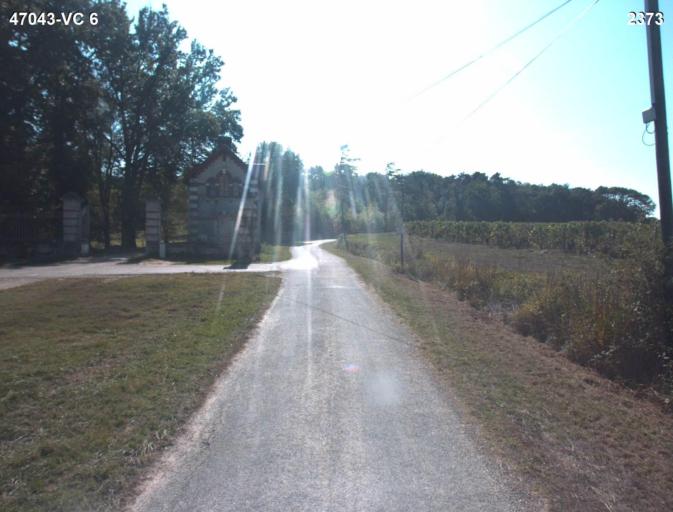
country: FR
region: Aquitaine
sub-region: Departement du Lot-et-Garonne
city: Buzet-sur-Baise
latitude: 44.2325
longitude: 0.2930
